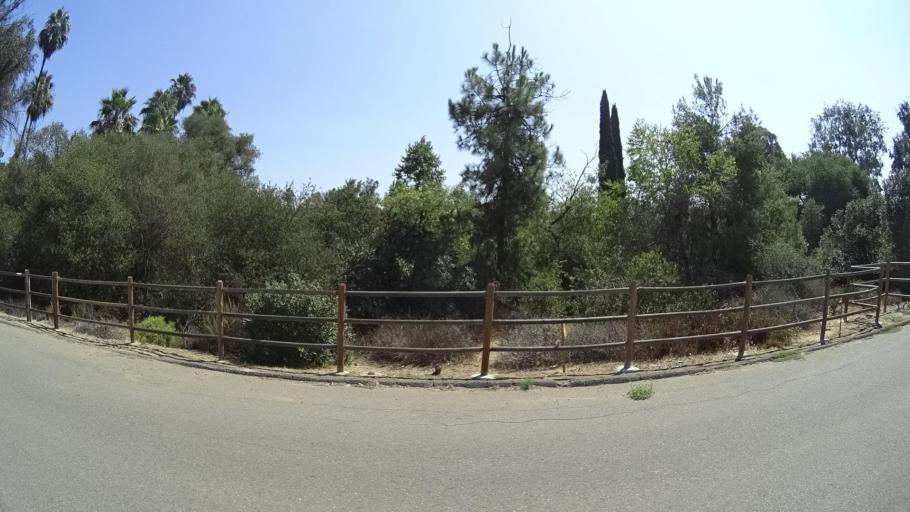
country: US
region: California
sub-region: San Diego County
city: Vista
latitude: 33.2397
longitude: -117.2413
